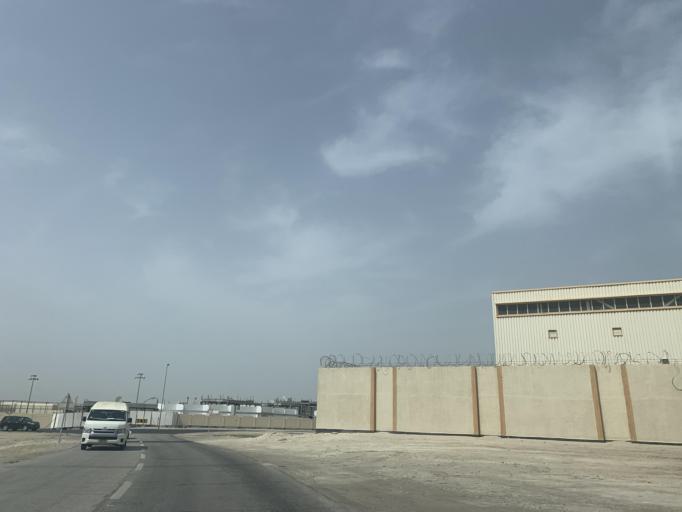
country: BH
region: Northern
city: Madinat `Isa
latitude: 26.1620
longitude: 50.5547
